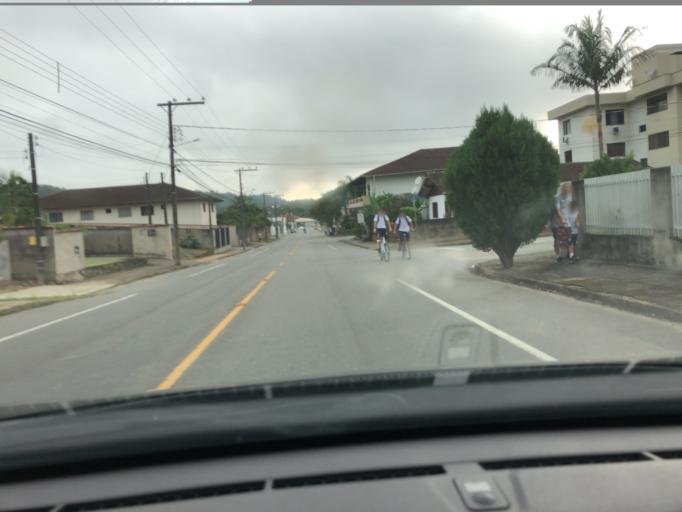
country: BR
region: Santa Catarina
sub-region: Jaragua Do Sul
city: Jaragua do Sul
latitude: -26.5093
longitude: -49.1374
